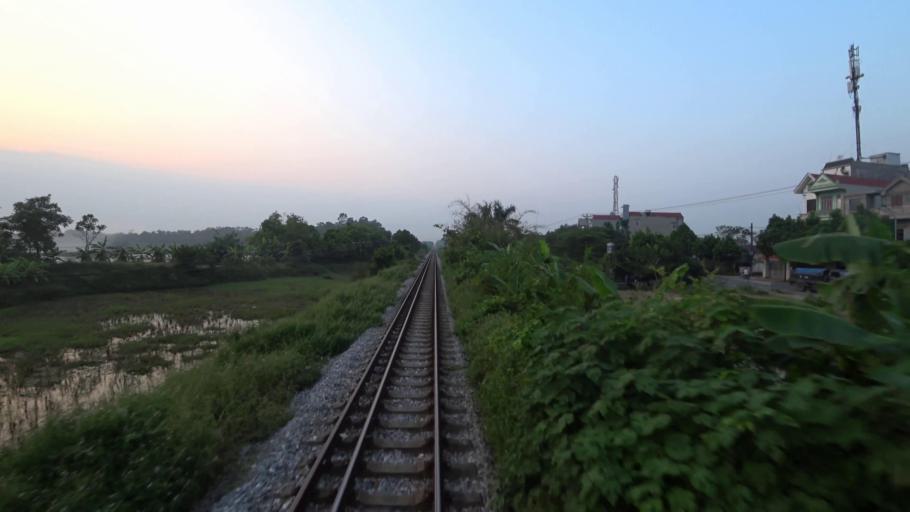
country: VN
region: Ha Noi
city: Dong Anh
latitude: 21.1314
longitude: 105.8750
